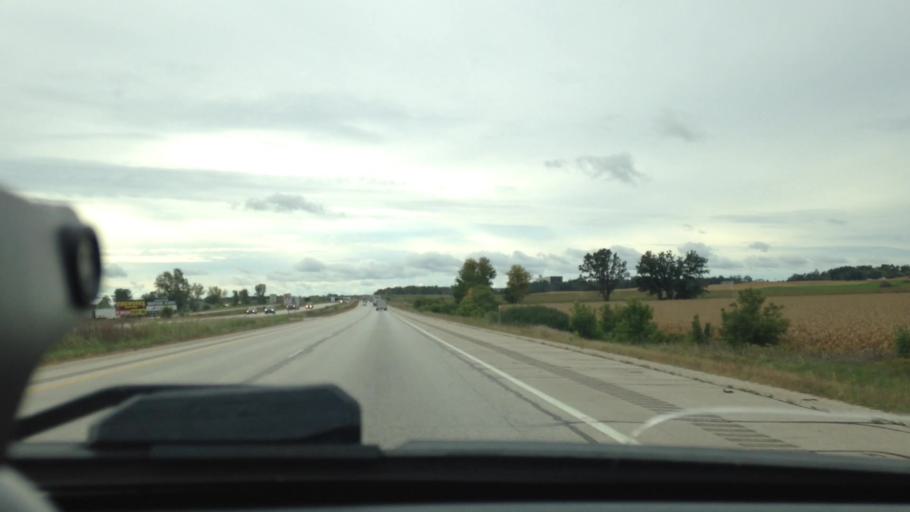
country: US
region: Wisconsin
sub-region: Dodge County
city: Lomira
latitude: 43.6479
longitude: -88.4421
